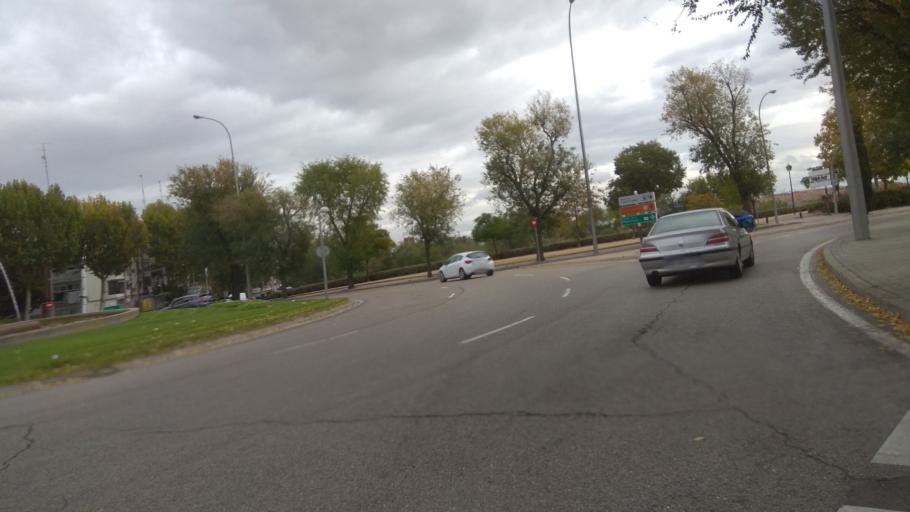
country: ES
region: Madrid
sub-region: Provincia de Madrid
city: Vicalvaro
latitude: 40.4055
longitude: -3.6175
